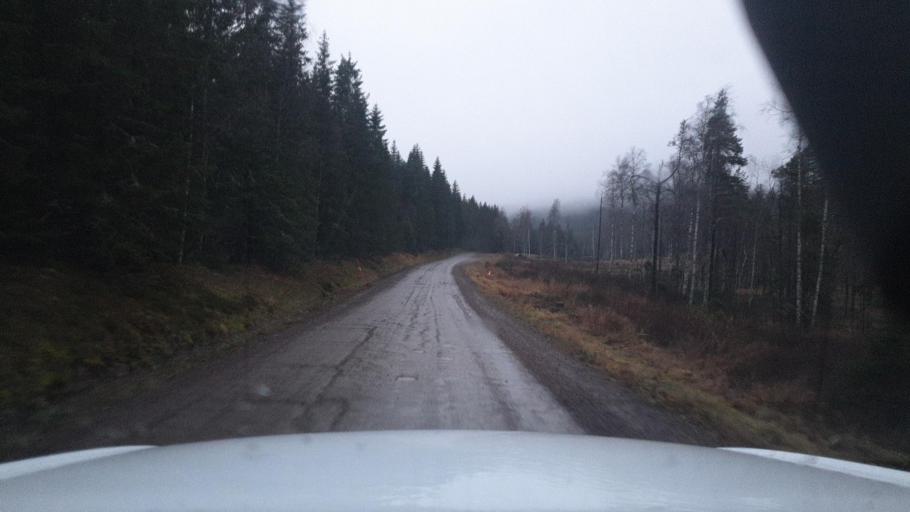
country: SE
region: Vaermland
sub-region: Sunne Kommun
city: Sunne
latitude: 59.8242
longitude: 12.8710
